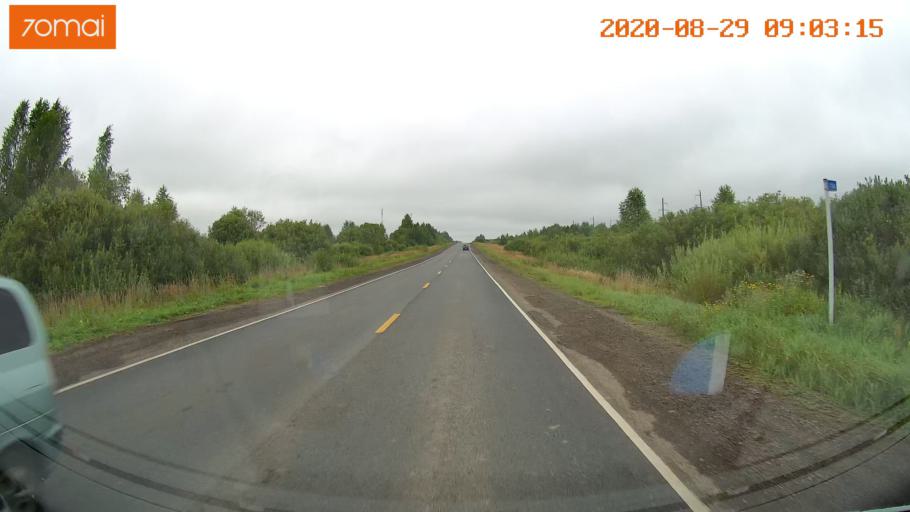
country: RU
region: Ivanovo
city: Staraya Vichuga
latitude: 57.3356
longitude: 41.9642
